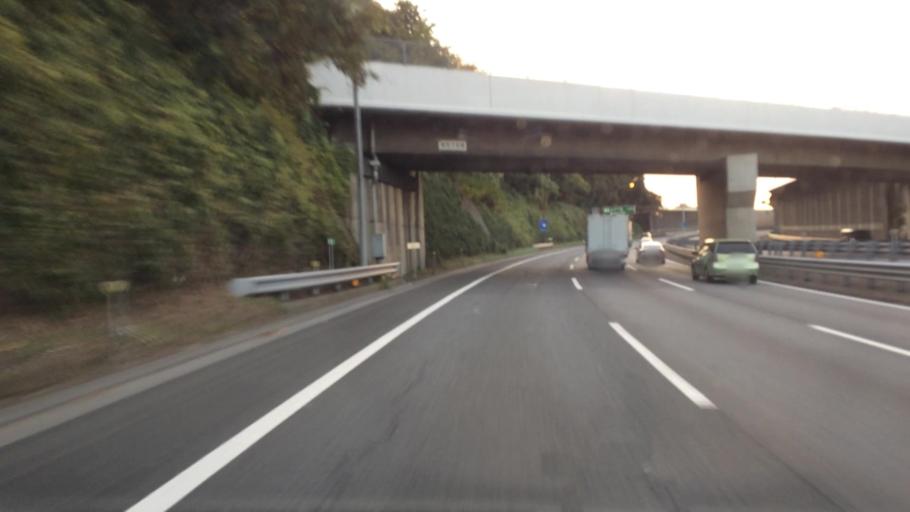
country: JP
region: Chiba
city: Chiba
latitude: 35.6418
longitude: 140.0771
